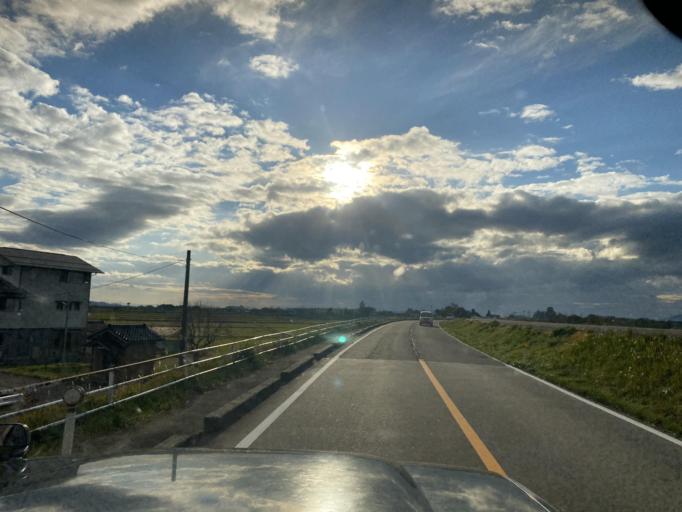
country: JP
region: Niigata
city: Kamo
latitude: 37.6846
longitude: 139.0259
